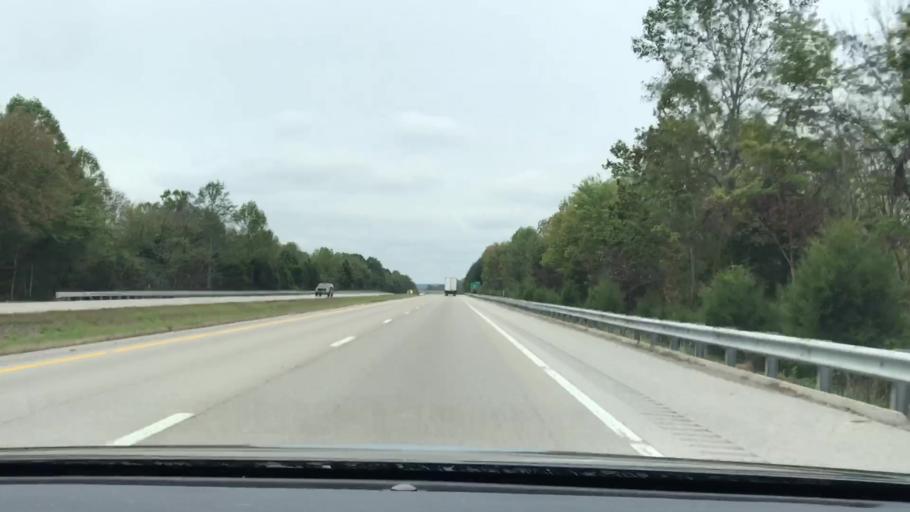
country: US
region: Kentucky
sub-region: Metcalfe County
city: Edmonton
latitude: 37.0055
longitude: -85.5955
